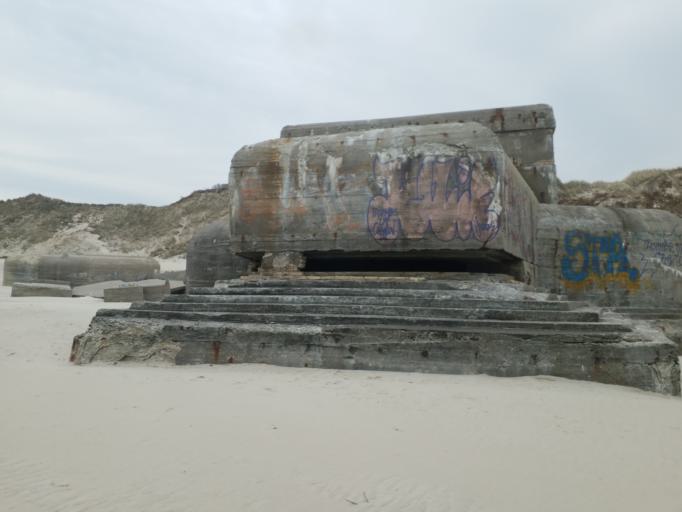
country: DK
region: North Denmark
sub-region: Jammerbugt Kommune
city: Pandrup
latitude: 57.3802
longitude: 9.7171
